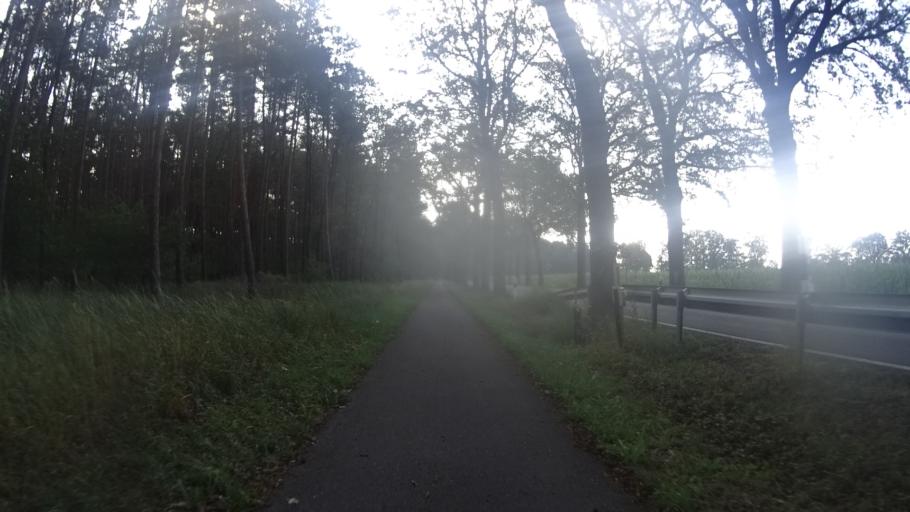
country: DE
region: Brandenburg
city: Cumlosen
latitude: 53.0207
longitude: 11.6974
